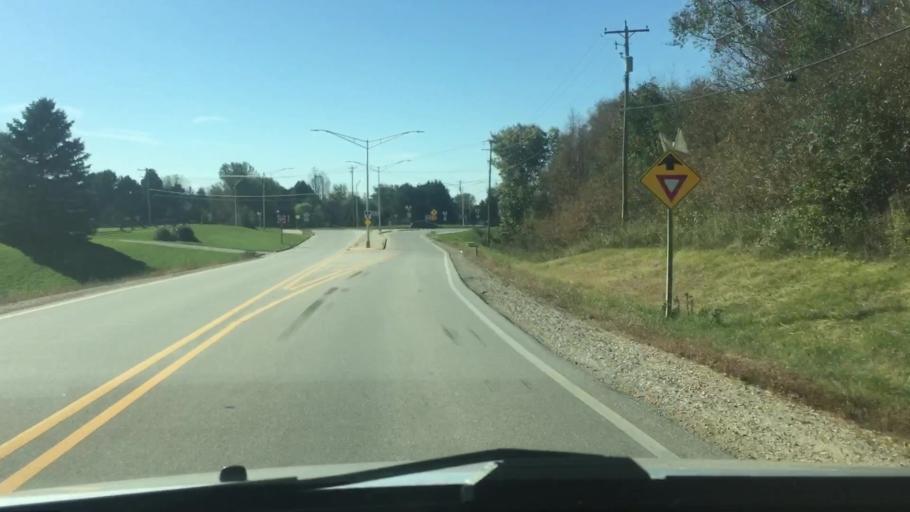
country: US
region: Wisconsin
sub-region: Waukesha County
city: Wales
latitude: 42.9894
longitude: -88.3784
